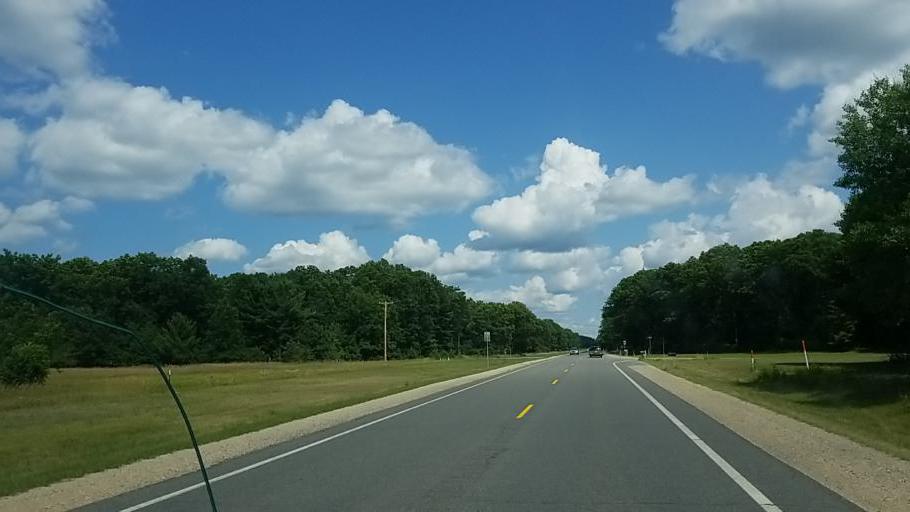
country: US
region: Michigan
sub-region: Newaygo County
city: Newaygo
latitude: 43.4058
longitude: -85.7038
